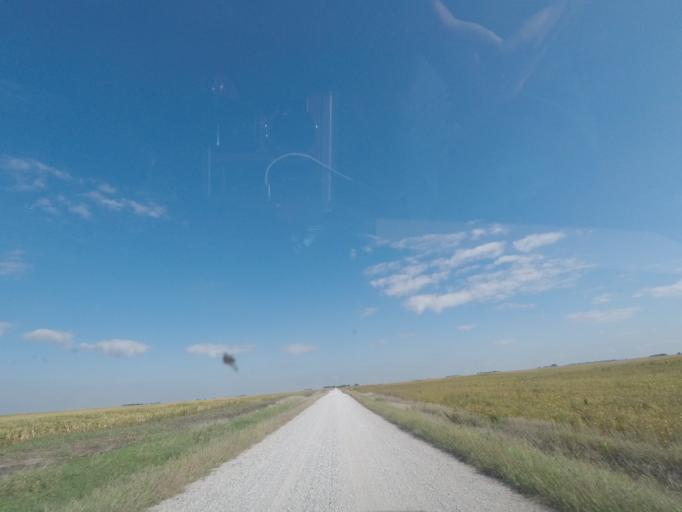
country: US
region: Iowa
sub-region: Story County
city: Nevada
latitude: 42.0392
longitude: -93.4252
